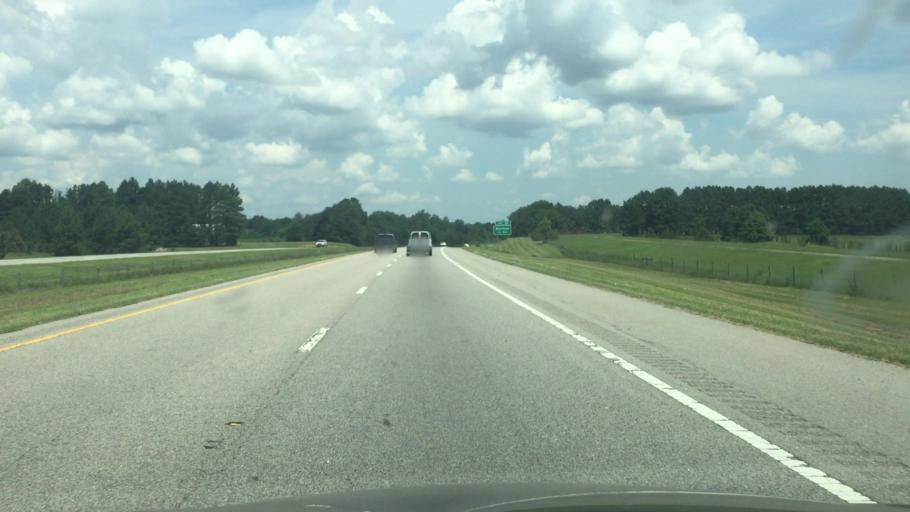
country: US
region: North Carolina
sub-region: Richmond County
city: Ellerbe
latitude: 35.1602
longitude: -79.7160
